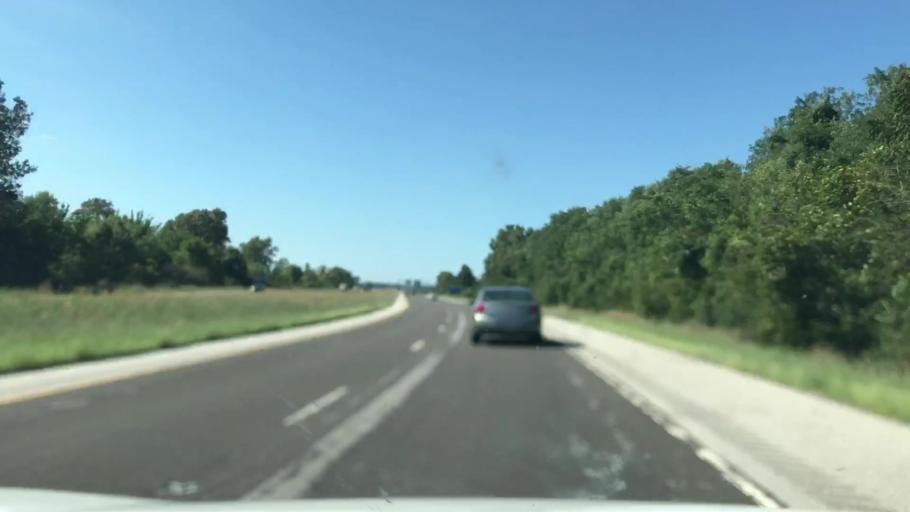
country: US
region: Illinois
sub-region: Madison County
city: South Roxana
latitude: 38.8416
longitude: -90.0444
